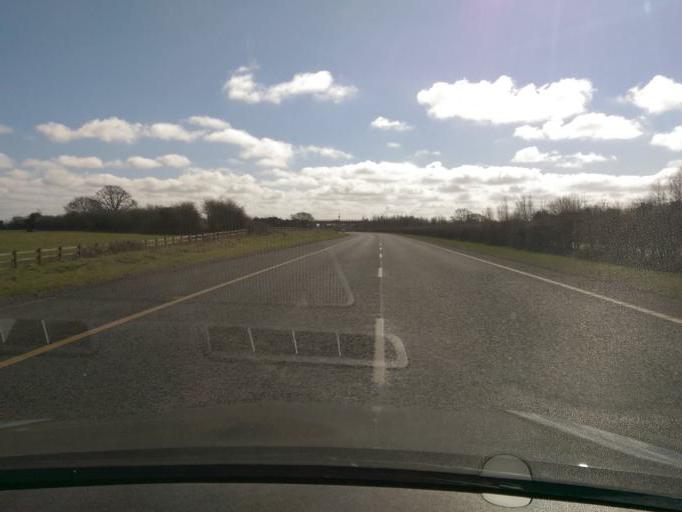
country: IE
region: Leinster
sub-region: An Mhi
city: Longwood
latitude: 53.4163
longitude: -6.9044
